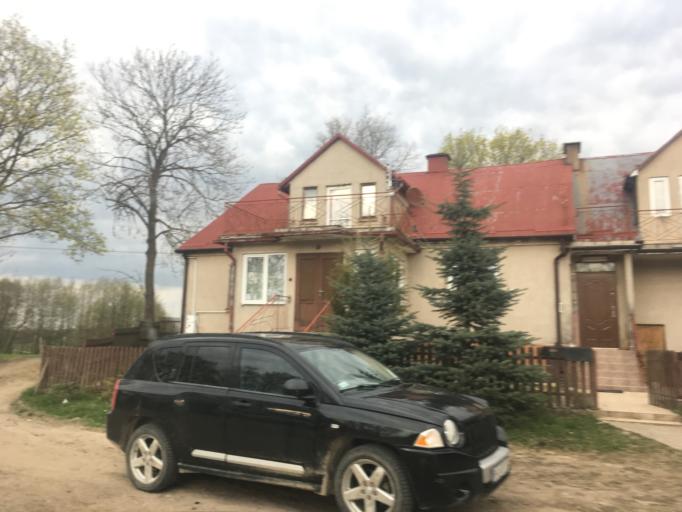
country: PL
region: Podlasie
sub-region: Powiat sejnenski
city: Punsk
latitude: 54.2875
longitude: 23.1002
